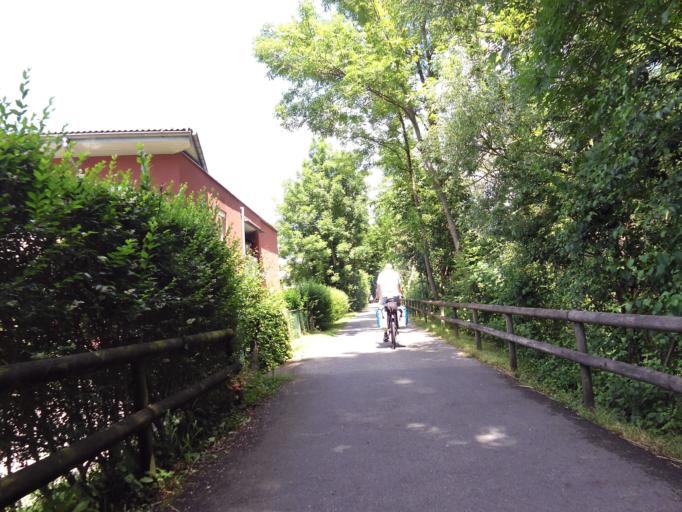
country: AT
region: Vorarlberg
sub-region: Politischer Bezirk Bregenz
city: Hard
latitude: 47.4985
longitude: 9.6982
